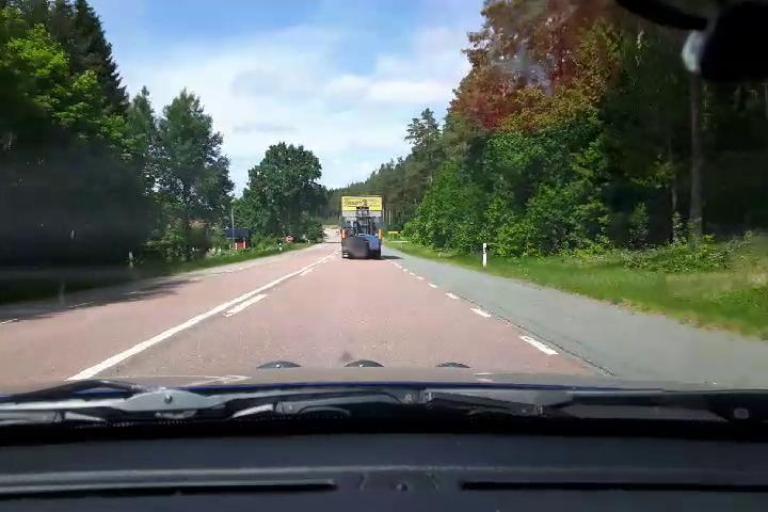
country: SE
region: Uppsala
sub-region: Osthammars Kommun
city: Bjorklinge
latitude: 60.1404
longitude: 17.5046
